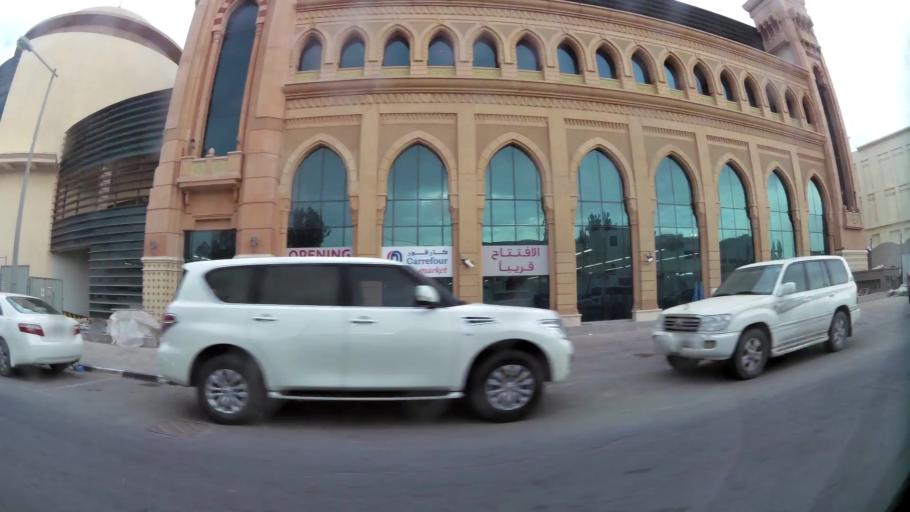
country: QA
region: Baladiyat ad Dawhah
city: Doha
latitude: 25.2727
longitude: 51.4991
